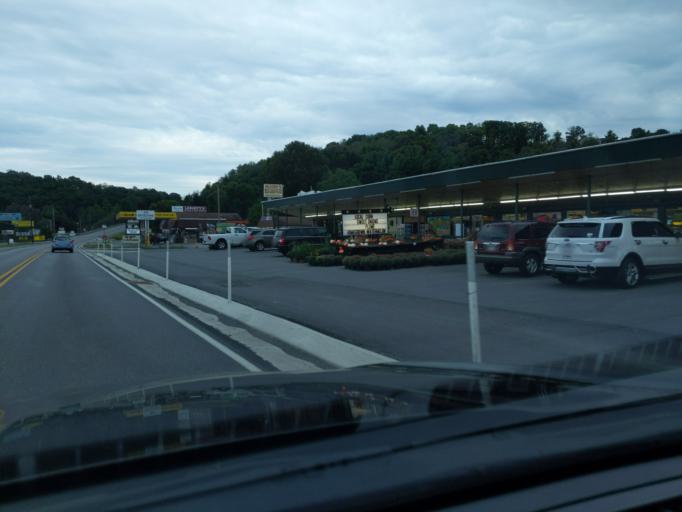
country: US
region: Pennsylvania
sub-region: Blair County
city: Duncansville
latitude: 40.3898
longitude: -78.4353
